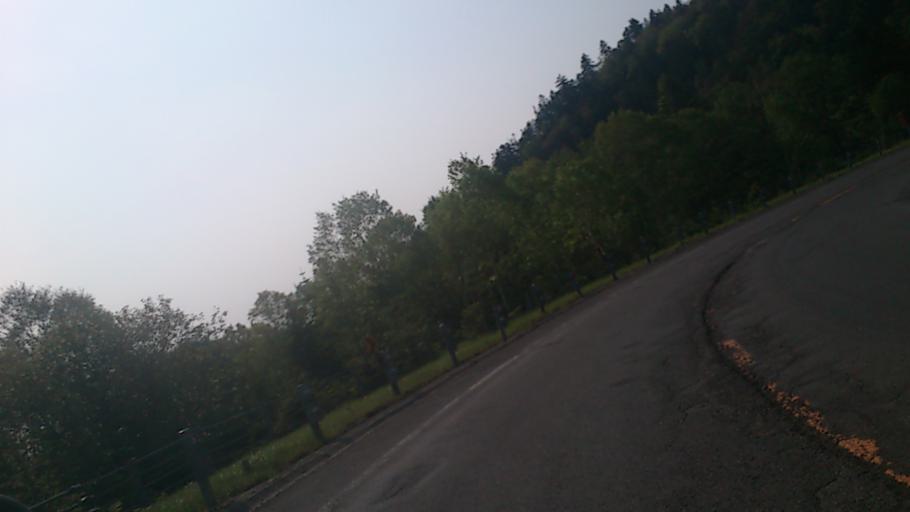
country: JP
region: Hokkaido
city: Bihoro
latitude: 43.4631
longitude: 144.2371
